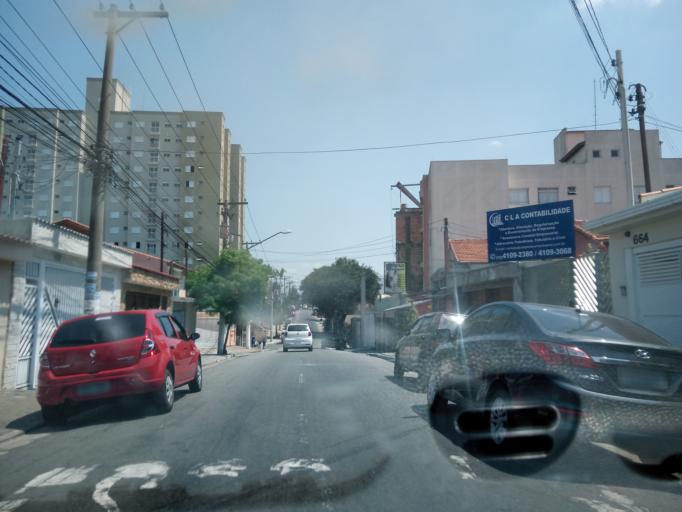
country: BR
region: Sao Paulo
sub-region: Sao Bernardo Do Campo
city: Sao Bernardo do Campo
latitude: -23.7205
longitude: -46.5696
